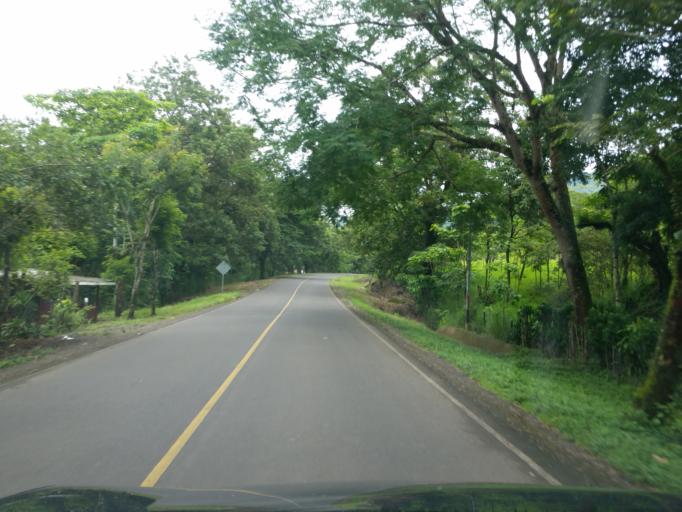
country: NI
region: Matagalpa
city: San Ramon
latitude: 13.0512
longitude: -85.7616
